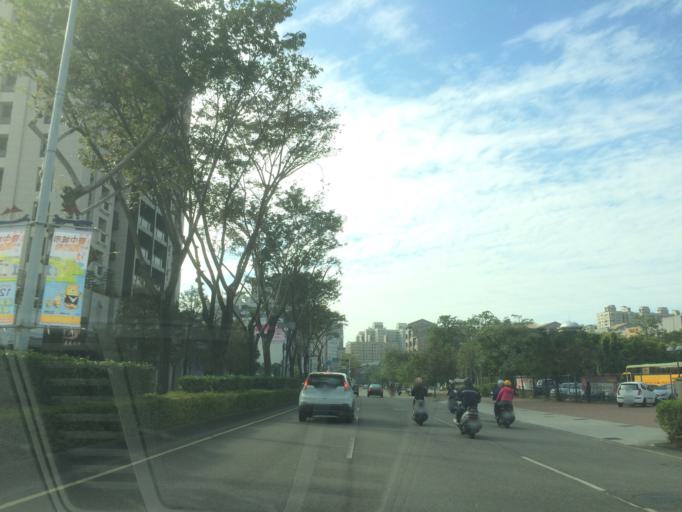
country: TW
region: Taiwan
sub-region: Taichung City
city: Taichung
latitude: 24.1512
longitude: 120.6423
